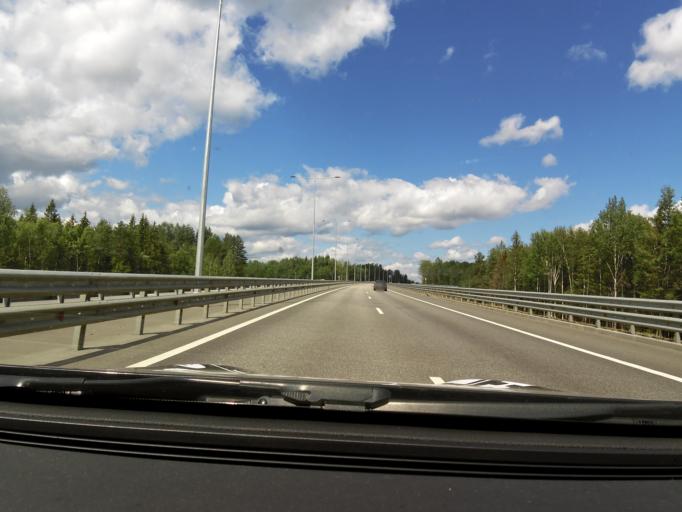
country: RU
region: Tverskaya
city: Vydropuzhsk
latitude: 57.2845
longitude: 34.7947
